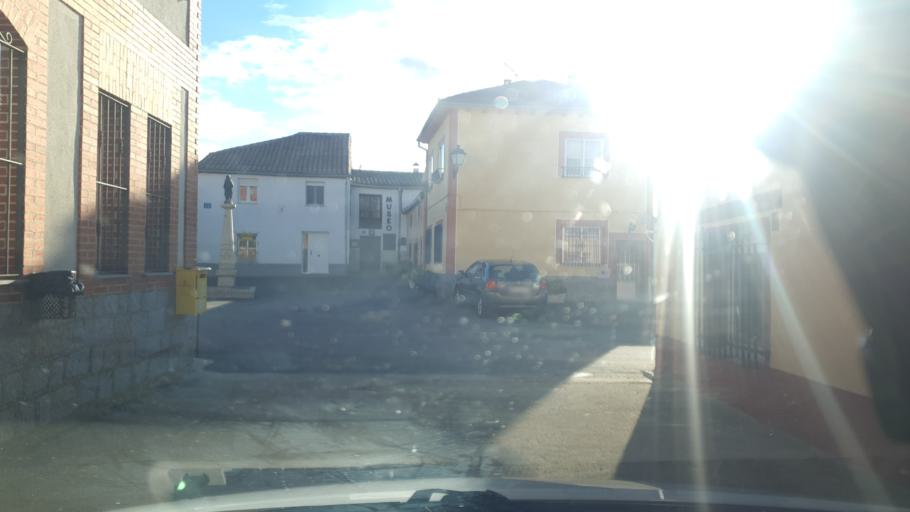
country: ES
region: Castille and Leon
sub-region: Provincia de Avila
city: Gotarrendura
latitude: 40.8266
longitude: -4.7409
